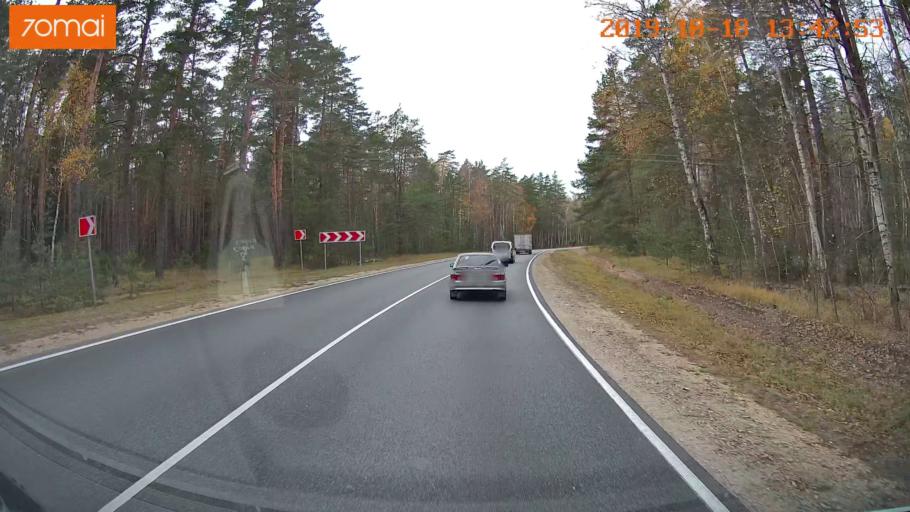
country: RU
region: Rjazan
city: Solotcha
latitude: 54.9270
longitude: 39.9817
